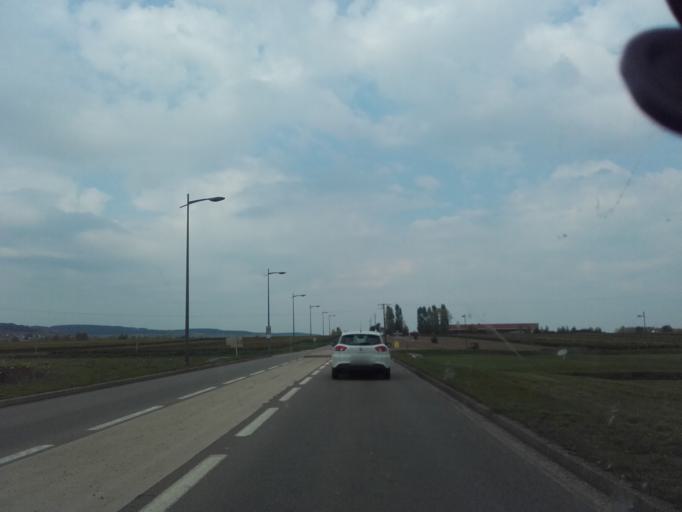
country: FR
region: Bourgogne
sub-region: Departement de la Cote-d'Or
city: Meursault
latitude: 46.9766
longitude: 4.7863
